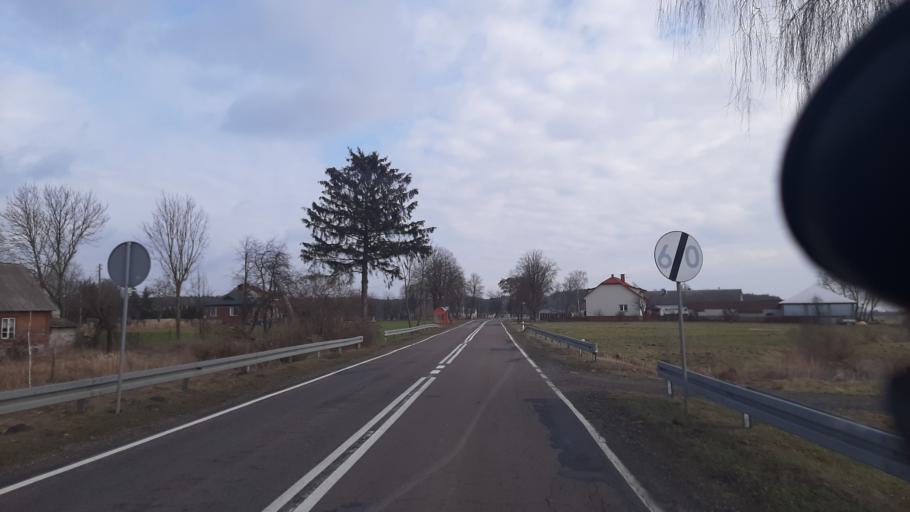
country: PL
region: Lublin Voivodeship
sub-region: Powiat lubartowski
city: Ostrow Lubelski
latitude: 51.4917
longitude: 22.7833
